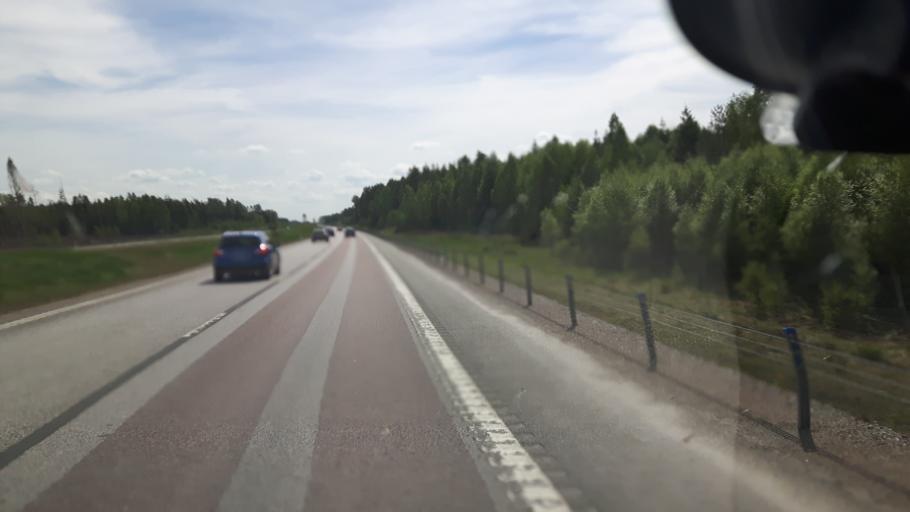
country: SE
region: Uppsala
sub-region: Tierps Kommun
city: Tierp
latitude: 60.2630
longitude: 17.4998
